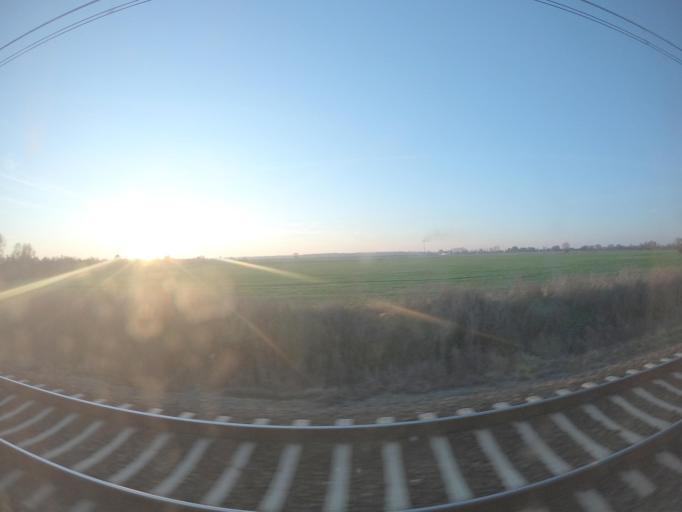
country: PL
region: Lubusz
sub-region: Powiat slubicki
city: Gorzyca
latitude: 52.5320
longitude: 14.6507
